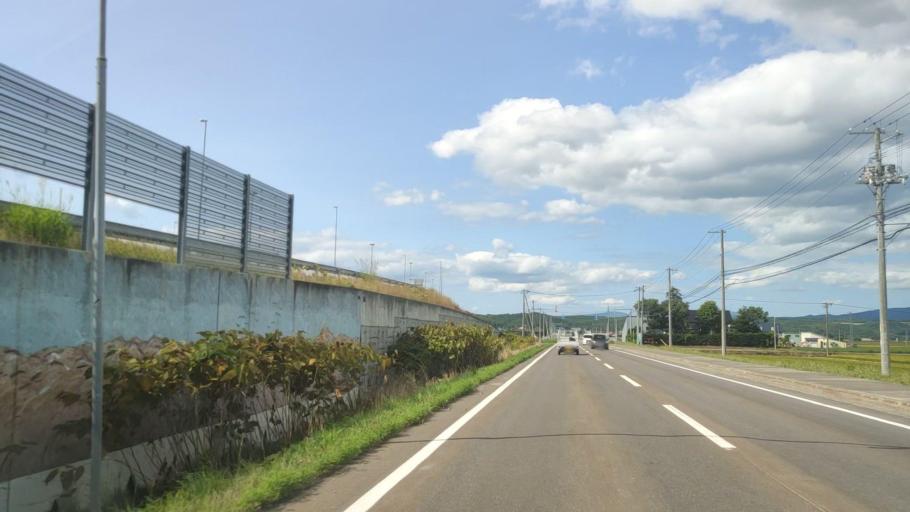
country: JP
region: Hokkaido
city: Nayoro
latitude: 44.3652
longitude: 142.4361
